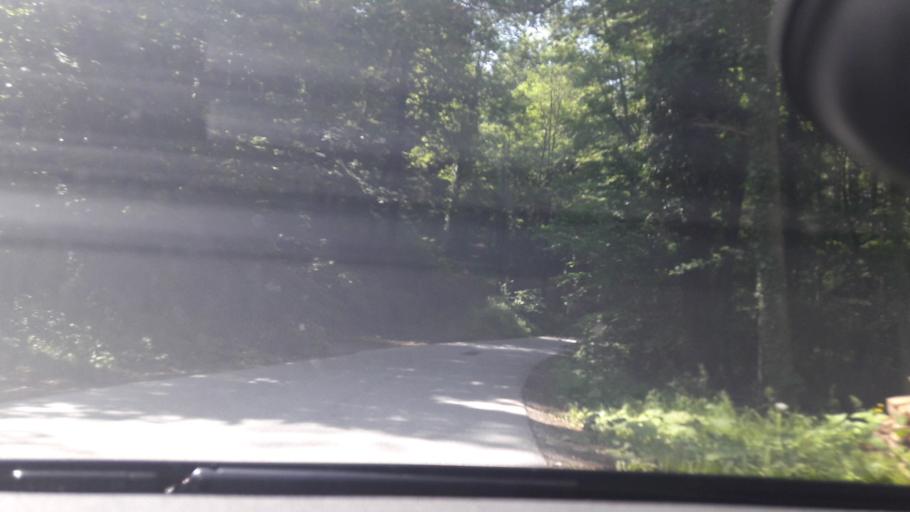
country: AT
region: Styria
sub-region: Politischer Bezirk Graz-Umgebung
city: Stiwoll
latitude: 47.1029
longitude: 15.1946
